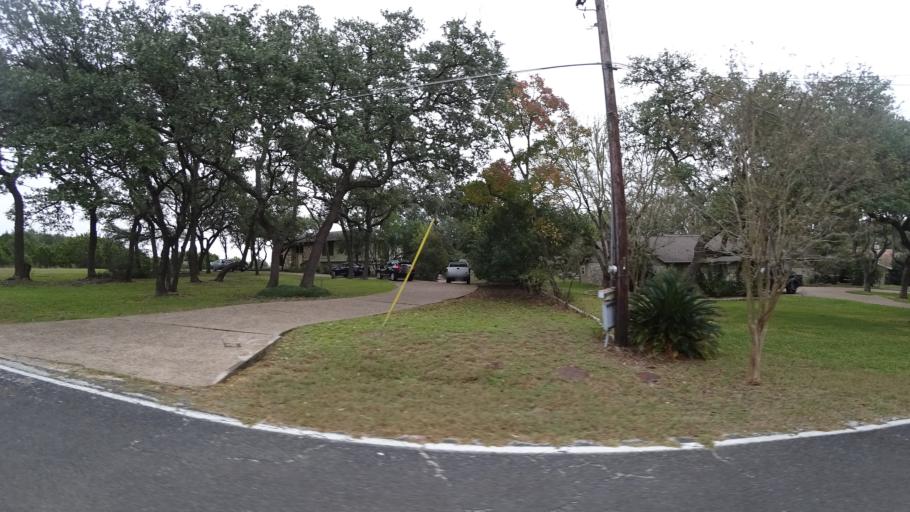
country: US
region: Texas
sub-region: Travis County
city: Barton Creek
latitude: 30.2299
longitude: -97.8980
